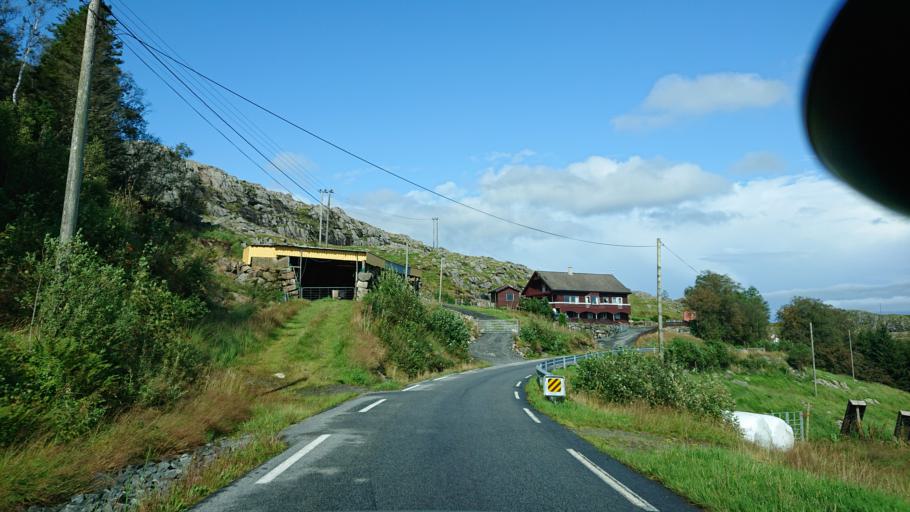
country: NO
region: Rogaland
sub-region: Gjesdal
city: Algard
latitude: 58.6958
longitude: 5.8843
